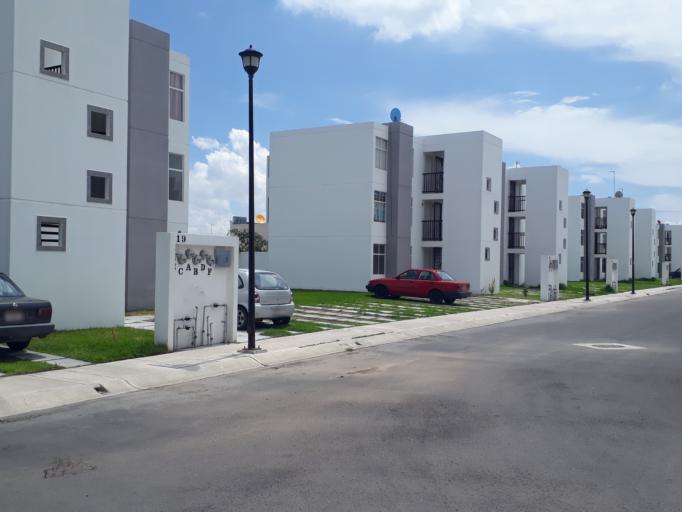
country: MX
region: Aguascalientes
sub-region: Aguascalientes
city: San Sebastian [Fraccionamiento]
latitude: 21.8080
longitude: -102.2701
